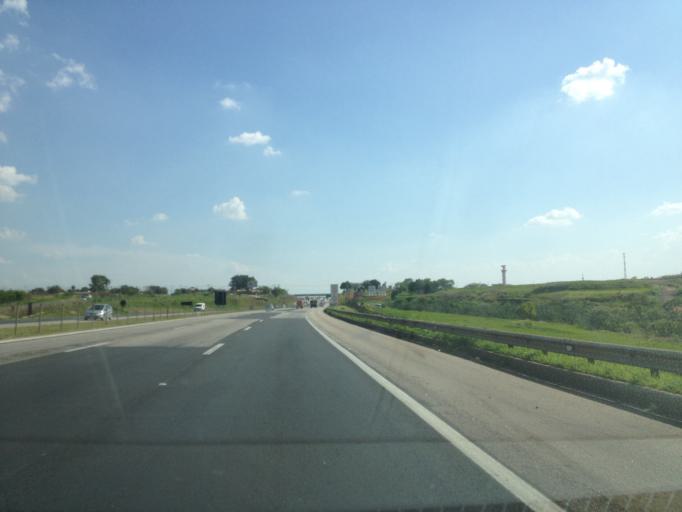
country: BR
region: Sao Paulo
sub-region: Indaiatuba
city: Indaiatuba
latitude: -23.0164
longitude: -47.1191
